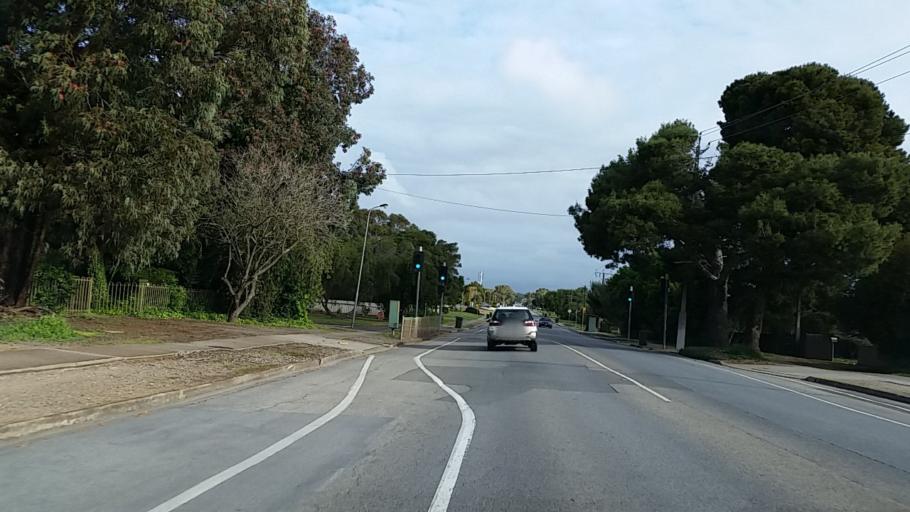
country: AU
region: South Australia
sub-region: Onkaparinga
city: Morphett Vale
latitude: -35.1304
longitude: 138.5367
